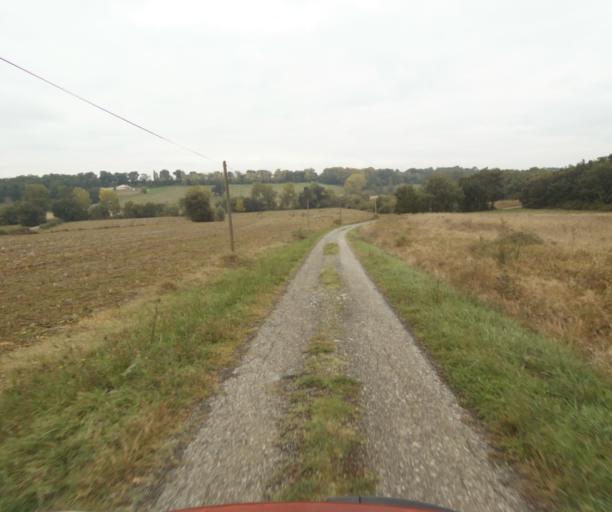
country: FR
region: Midi-Pyrenees
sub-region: Departement de la Haute-Garonne
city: Launac
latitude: 43.7967
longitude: 1.2106
